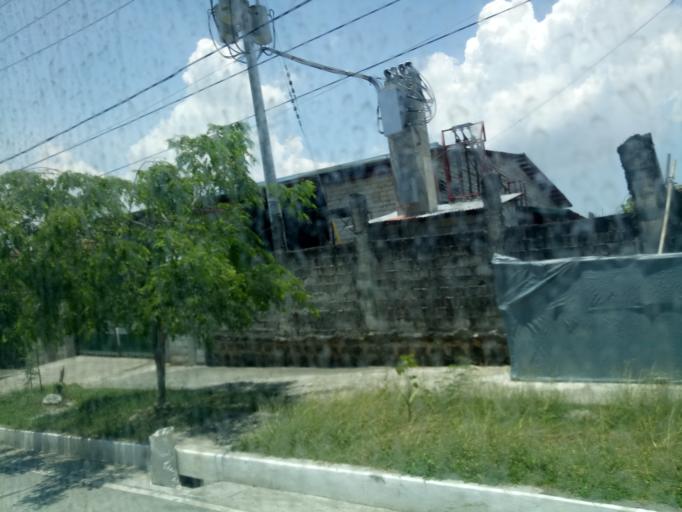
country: PH
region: Calabarzon
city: Bagong Pagasa
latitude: 14.7292
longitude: 121.0473
